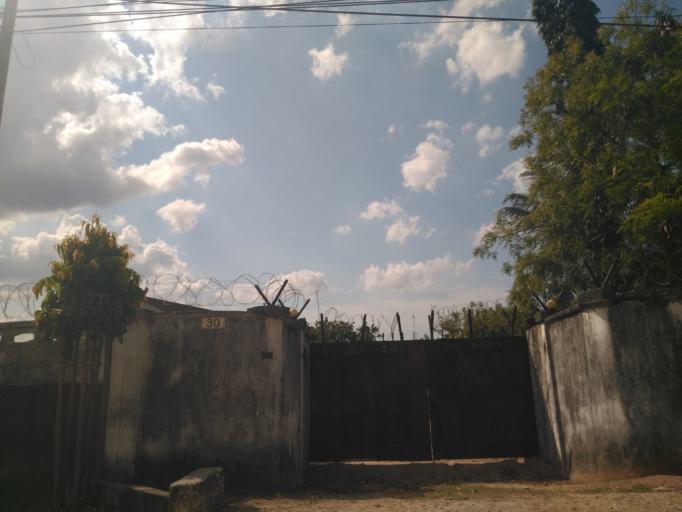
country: TZ
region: Dar es Salaam
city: Magomeni
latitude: -6.7741
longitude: 39.2581
